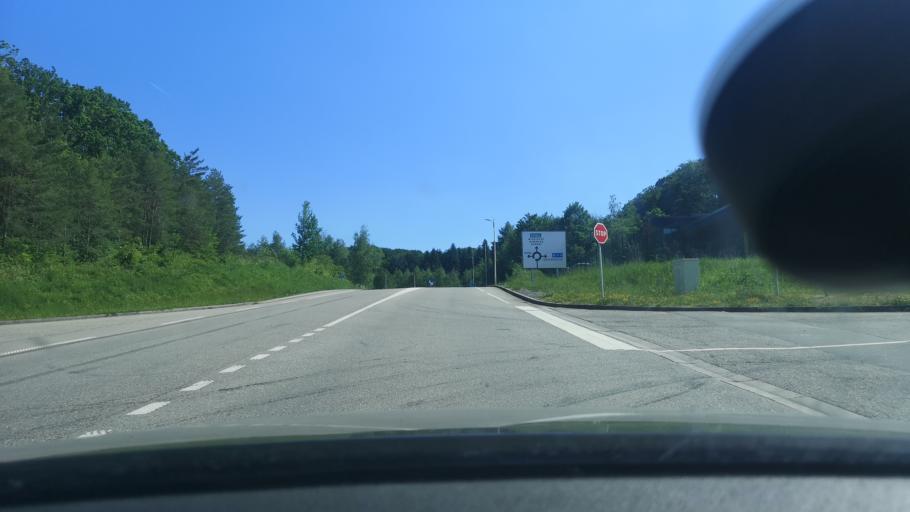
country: FR
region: Lorraine
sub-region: Departement des Vosges
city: Vittel
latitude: 48.1956
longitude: 5.9290
